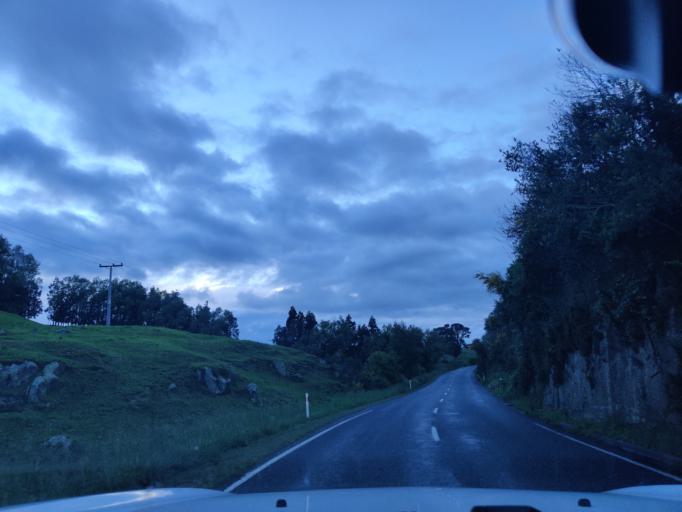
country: NZ
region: Waikato
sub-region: South Waikato District
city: Tokoroa
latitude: -38.1909
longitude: 175.7992
